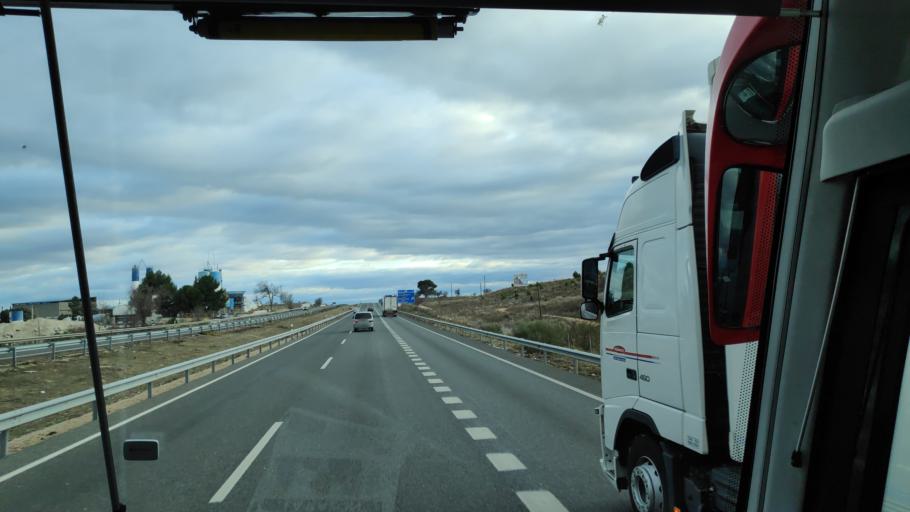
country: ES
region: Madrid
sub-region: Provincia de Madrid
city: Villarejo de Salvanes
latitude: 40.1861
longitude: -3.2982
